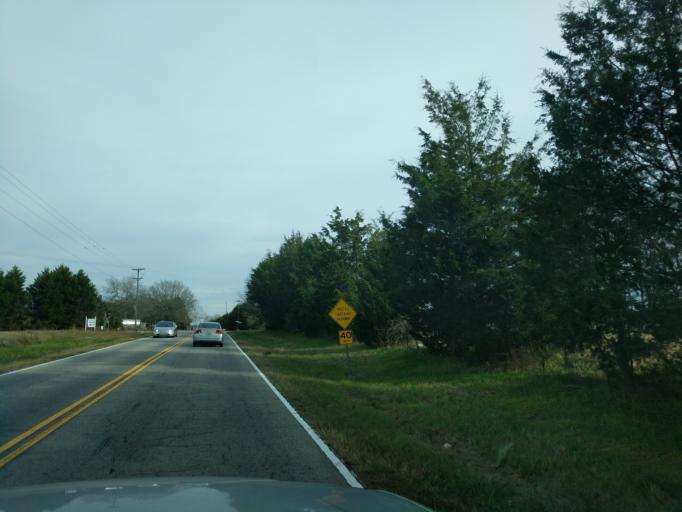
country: US
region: South Carolina
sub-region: Pickens County
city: Central
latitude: 34.7032
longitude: -82.7232
